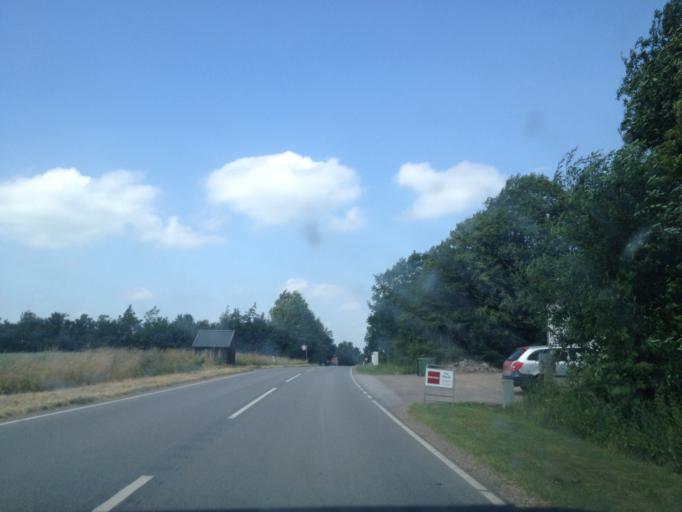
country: DK
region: South Denmark
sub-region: Kolding Kommune
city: Vamdrup
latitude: 55.3750
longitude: 9.2779
